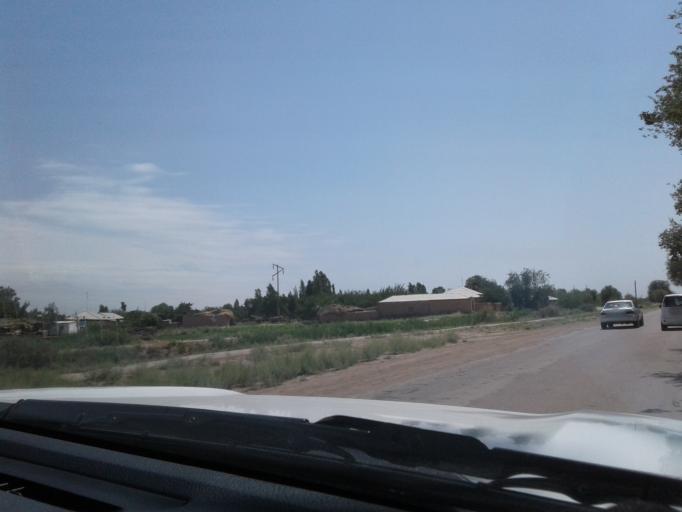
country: TM
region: Dasoguz
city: Tagta
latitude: 41.6209
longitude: 59.9744
